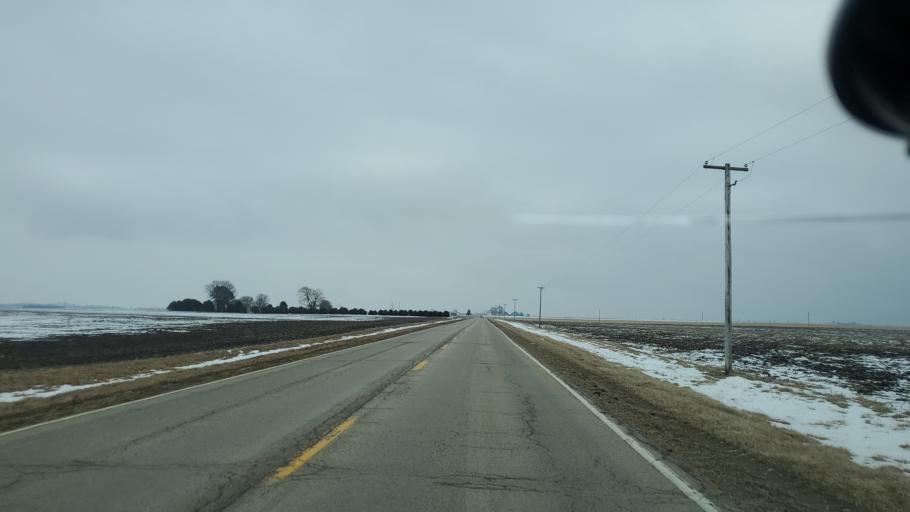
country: US
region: Illinois
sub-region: Marshall County
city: Wenona
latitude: 41.1188
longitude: -89.1098
